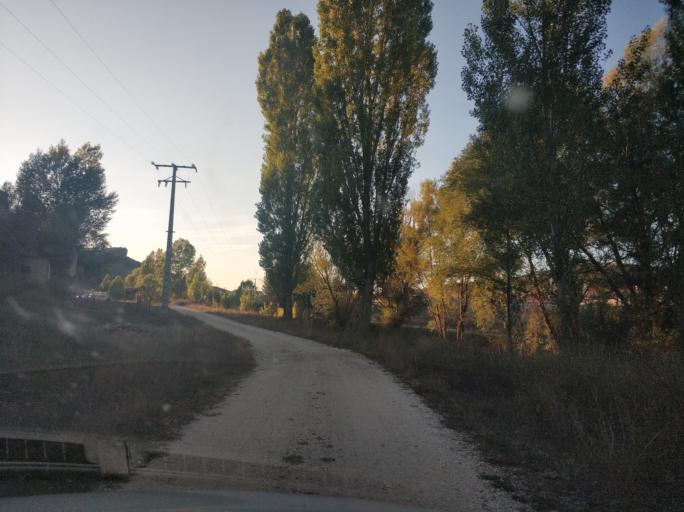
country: ES
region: Castille and Leon
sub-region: Provincia de Burgos
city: Hontoria del Pinar
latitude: 41.8437
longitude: -3.1619
